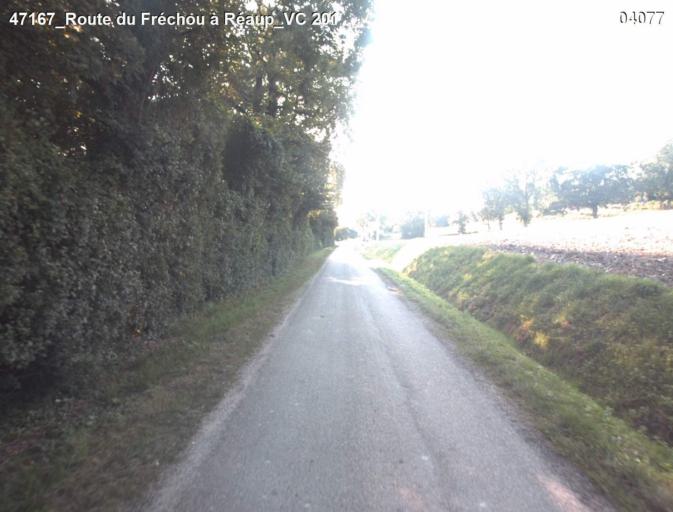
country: FR
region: Aquitaine
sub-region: Departement du Lot-et-Garonne
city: Mezin
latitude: 44.0726
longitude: 0.2673
